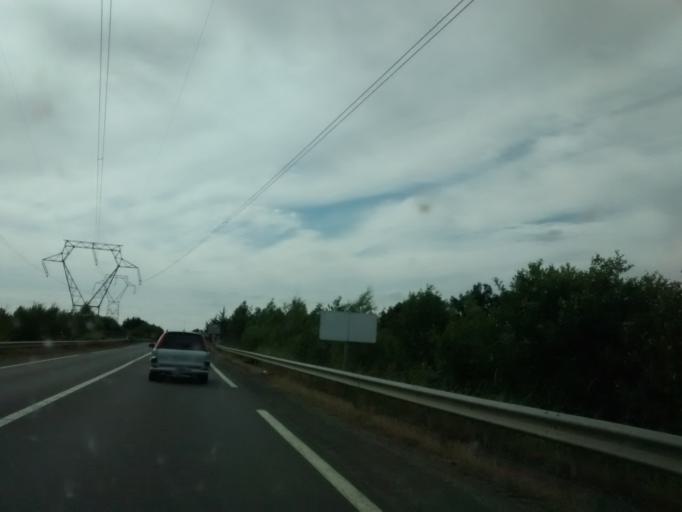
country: FR
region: Brittany
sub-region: Departement d'Ille-et-Vilaine
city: Betton
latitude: 48.1590
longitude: -1.6462
